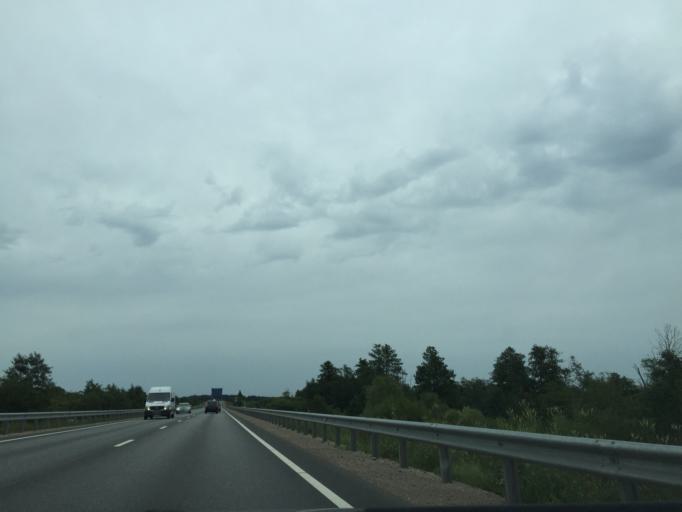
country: LV
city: Tireli
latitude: 56.8337
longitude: 23.5637
